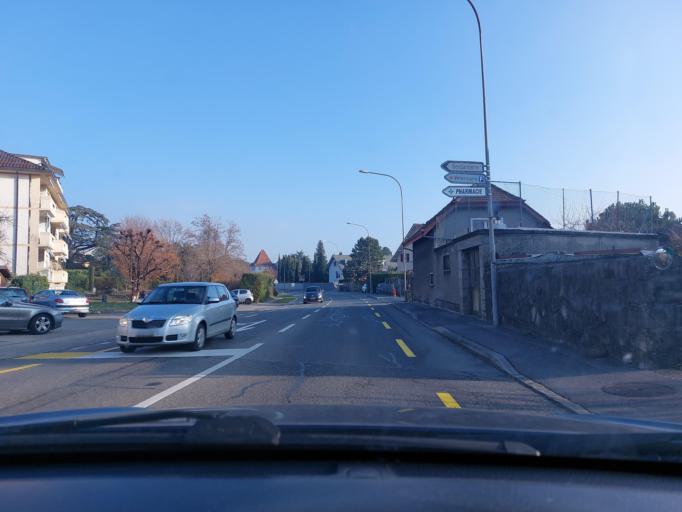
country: CH
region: Vaud
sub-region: Lavaux-Oron District
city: Paudex
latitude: 46.5056
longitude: 6.6712
